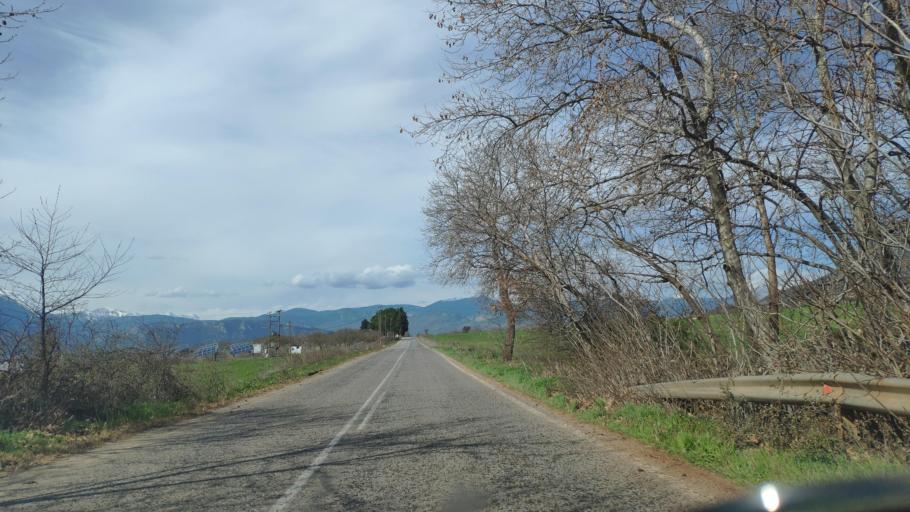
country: GR
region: Central Greece
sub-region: Nomos Fthiotidos
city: Amfikleia
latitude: 38.7063
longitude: 22.5018
